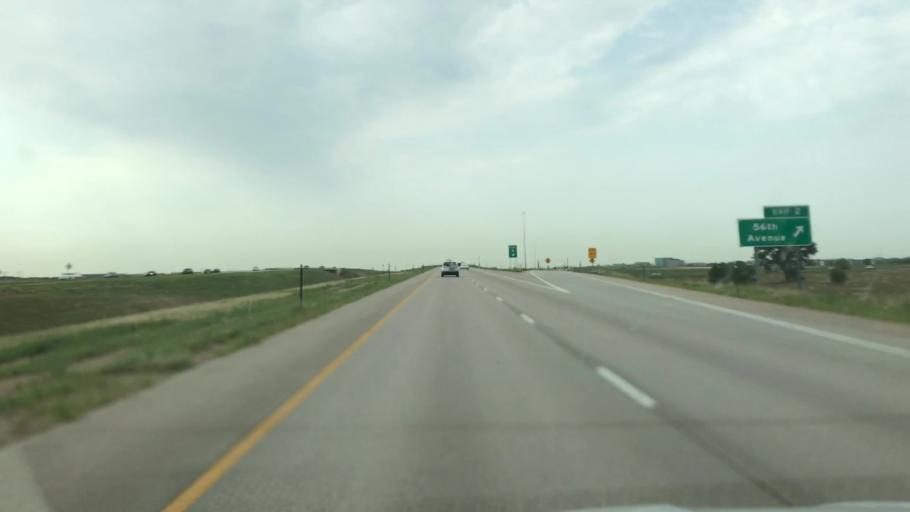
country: US
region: Colorado
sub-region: Adams County
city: Aurora
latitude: 39.8024
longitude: -104.7873
